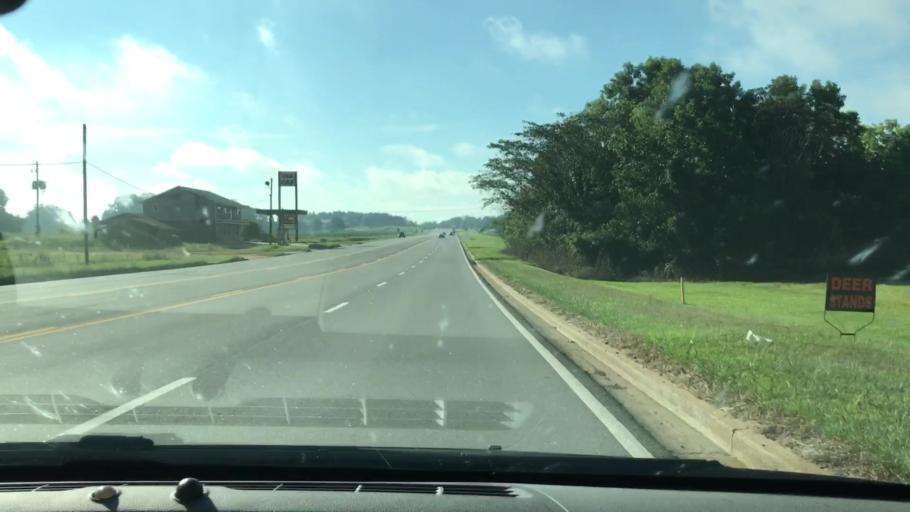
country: US
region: Georgia
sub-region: Terrell County
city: Dawson
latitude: 31.7179
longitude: -84.3477
